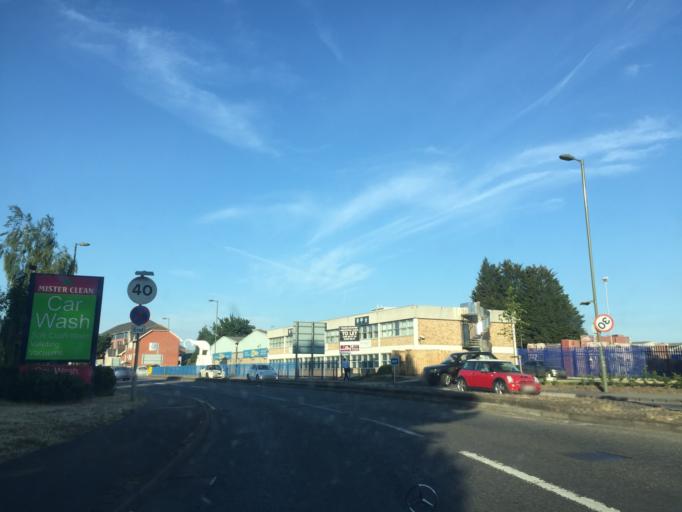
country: GB
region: England
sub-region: Bracknell Forest
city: Sandhurst
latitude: 51.3330
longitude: -0.7727
